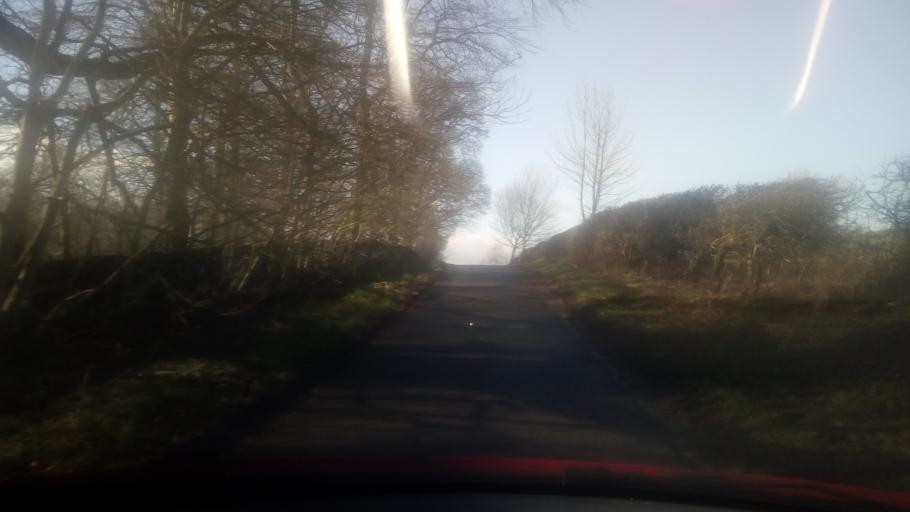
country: GB
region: Scotland
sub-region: The Scottish Borders
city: Jedburgh
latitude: 55.5227
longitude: -2.5958
